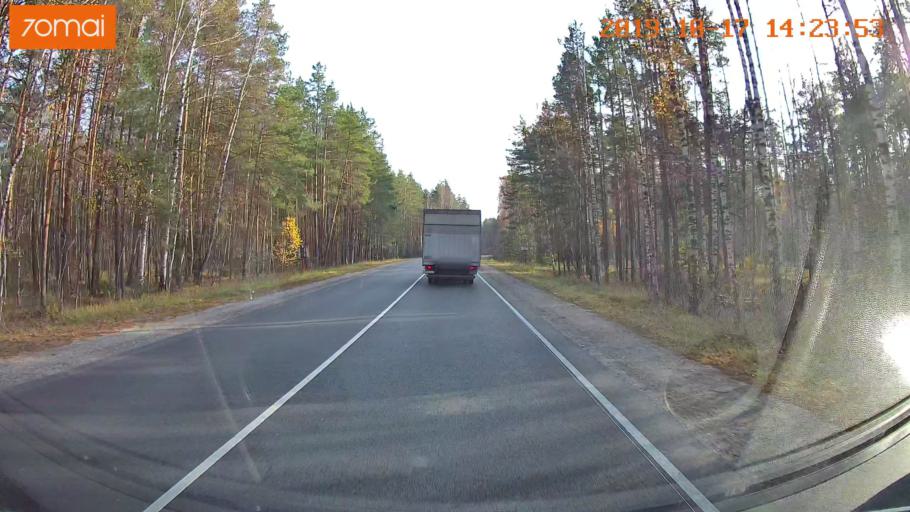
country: RU
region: Moskovskaya
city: Radovitskiy
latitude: 55.0143
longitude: 39.9631
